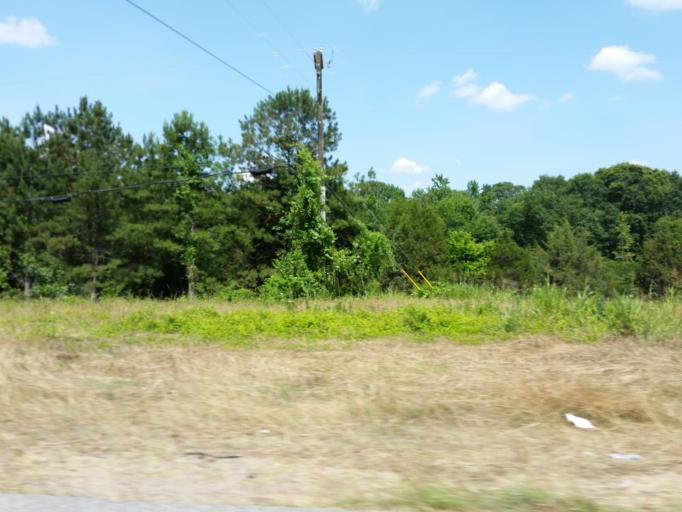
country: US
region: Alabama
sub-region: Marengo County
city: Demopolis
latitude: 32.5579
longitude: -87.8342
